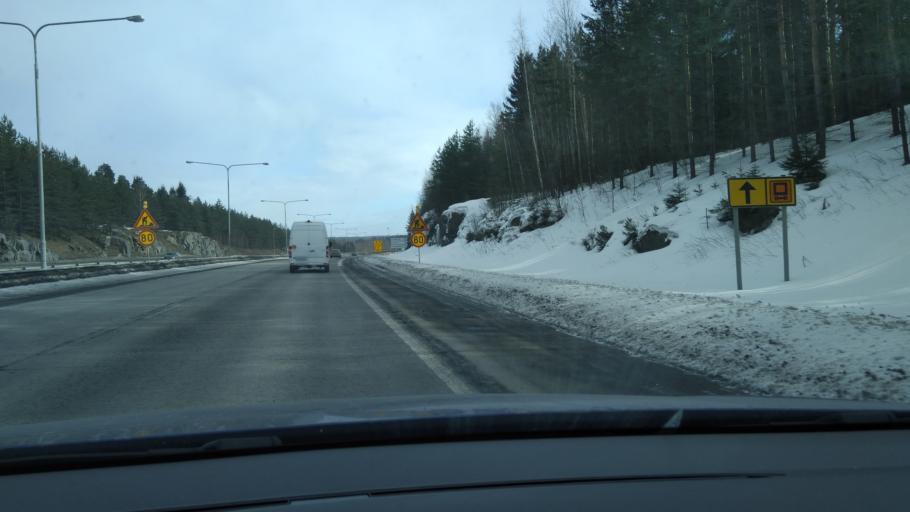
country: FI
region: Pirkanmaa
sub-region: Tampere
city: Tampere
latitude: 61.4689
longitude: 23.8239
